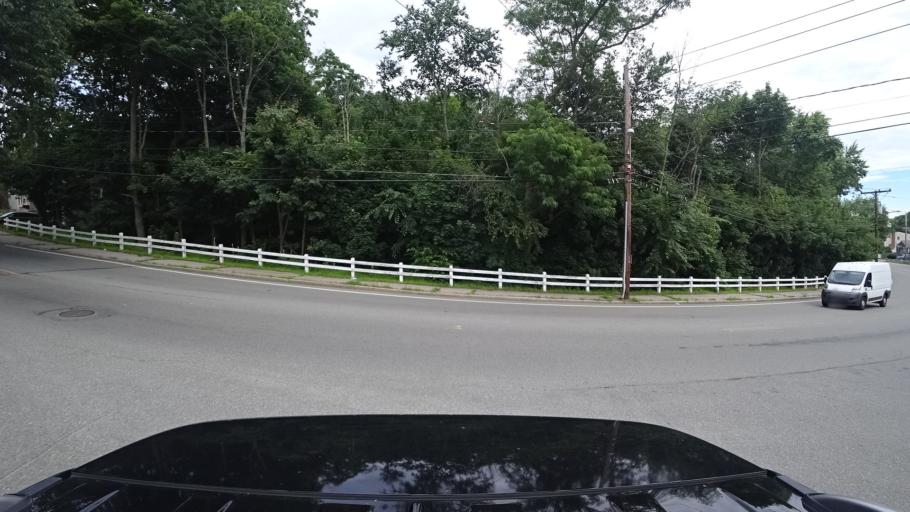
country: US
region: Massachusetts
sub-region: Norfolk County
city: Dedham
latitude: 42.2307
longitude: -71.1424
